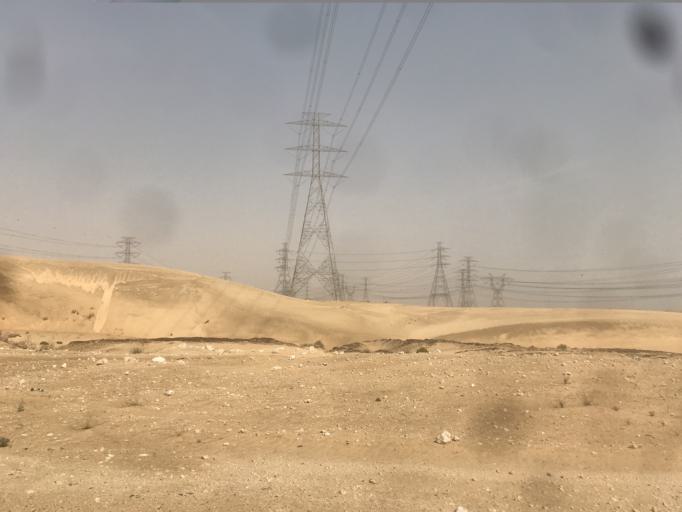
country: SA
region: Eastern Province
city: Abqaiq
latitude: 25.9071
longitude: 49.9062
